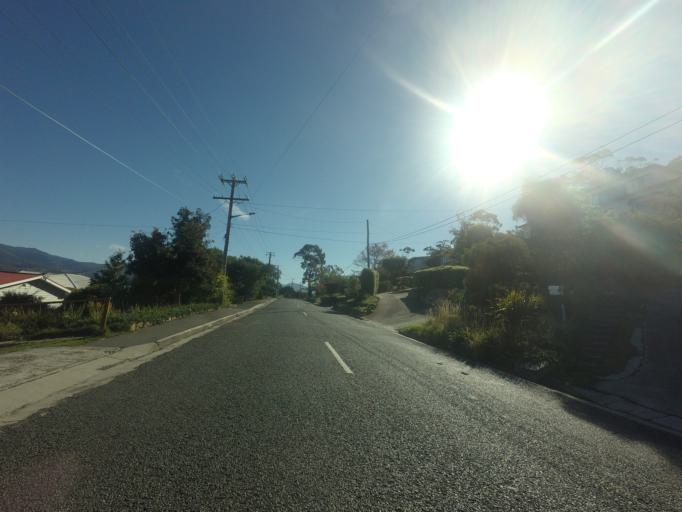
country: AU
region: Tasmania
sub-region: Clarence
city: Lindisfarne
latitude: -42.8462
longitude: 147.3415
